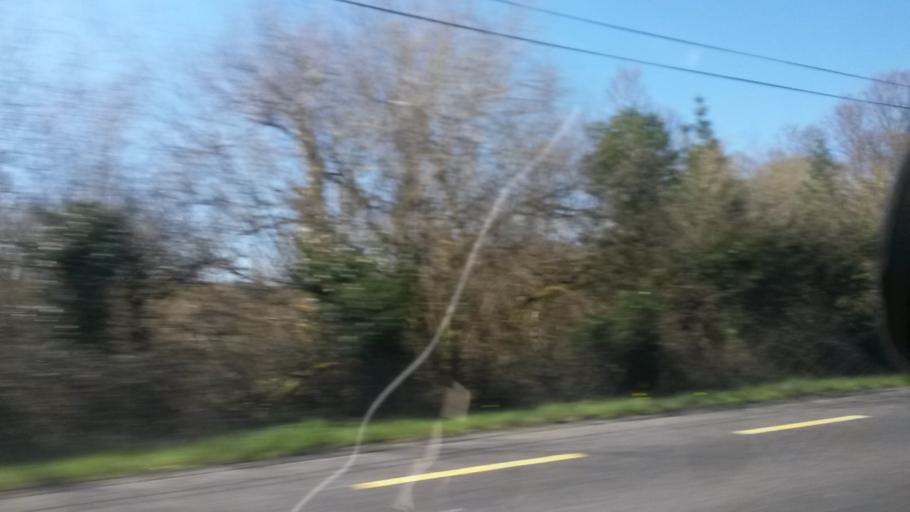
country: IE
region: Munster
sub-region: County Cork
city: Macroom
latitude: 51.9099
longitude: -9.0164
